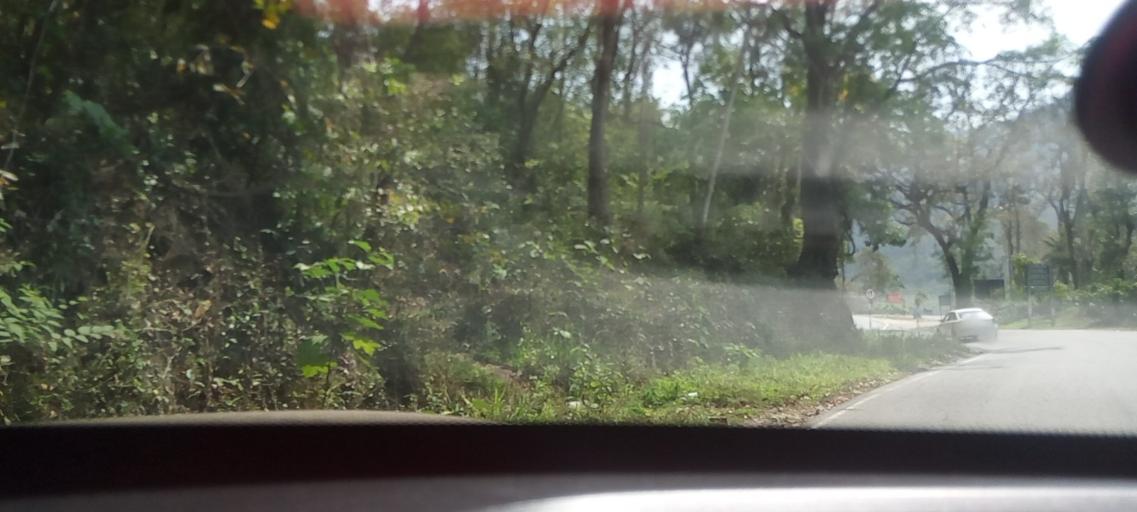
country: IN
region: Karnataka
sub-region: Chikmagalur
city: Mudigere
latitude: 13.2726
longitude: 75.6123
